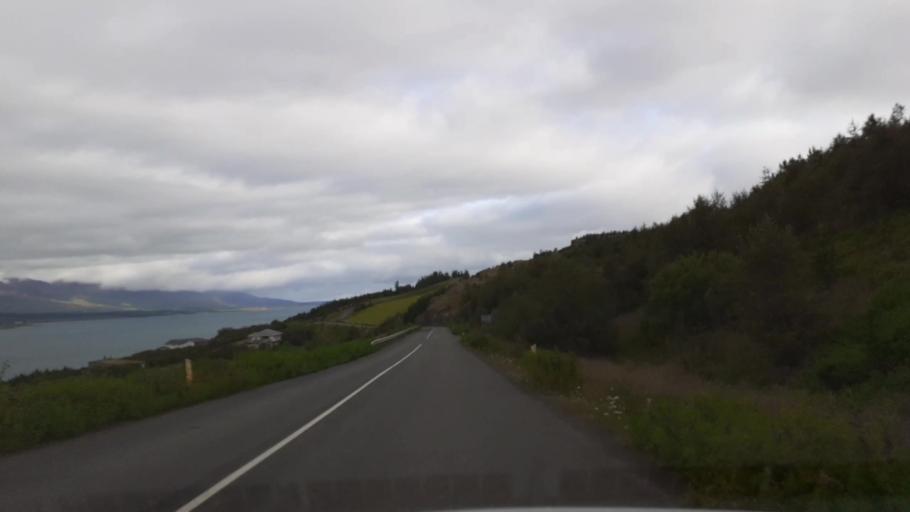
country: IS
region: Northeast
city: Akureyri
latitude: 65.6809
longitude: -18.0417
